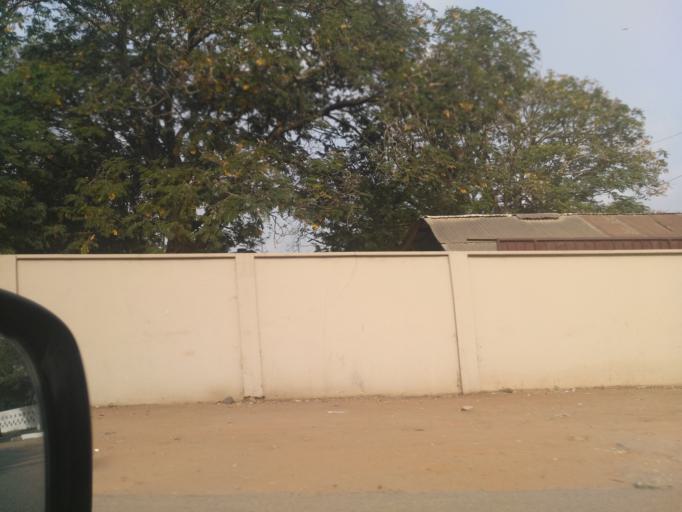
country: GH
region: Greater Accra
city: Accra
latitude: 5.6094
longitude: -0.1840
